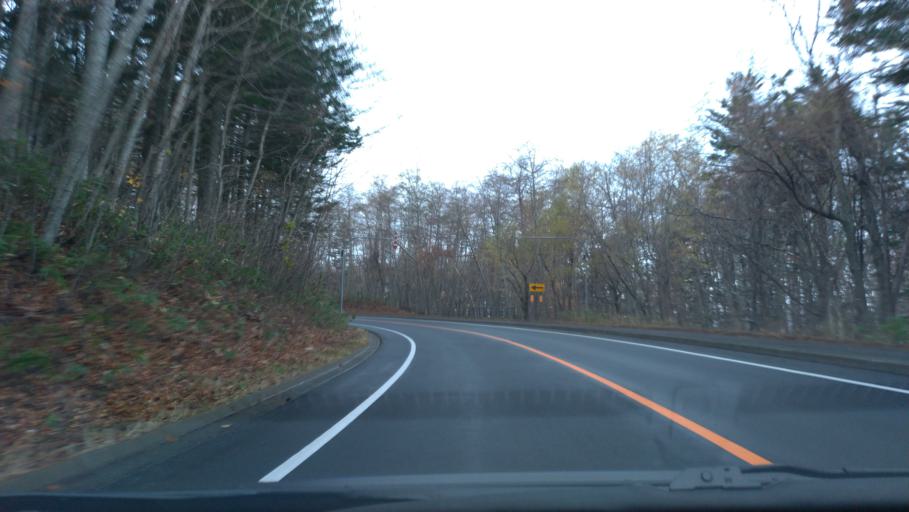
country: JP
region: Hokkaido
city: Shiraoi
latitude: 42.7351
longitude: 141.3728
